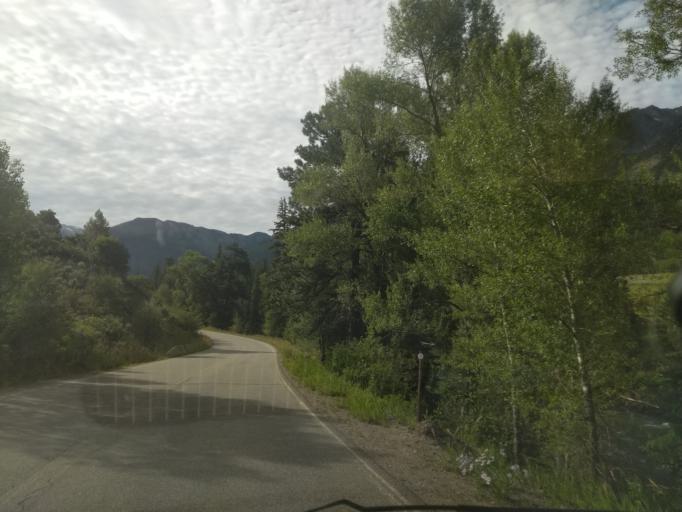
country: US
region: Colorado
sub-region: Garfield County
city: Carbondale
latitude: 39.0836
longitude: -107.2365
